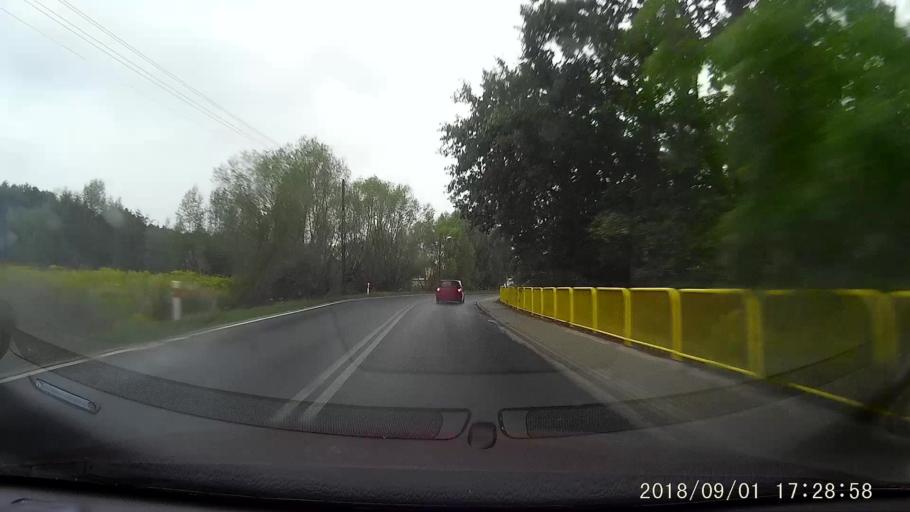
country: PL
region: Lubusz
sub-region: Powiat zaganski
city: Zagan
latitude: 51.6539
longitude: 15.3161
